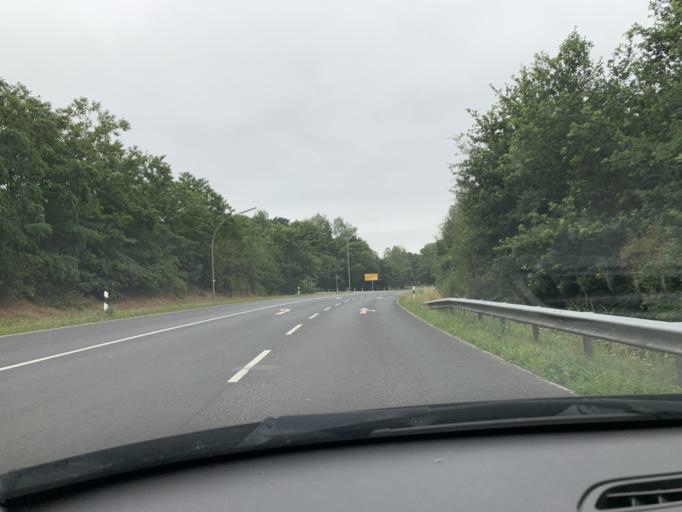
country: DE
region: Lower Saxony
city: Lingen
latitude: 52.4937
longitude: 7.2971
